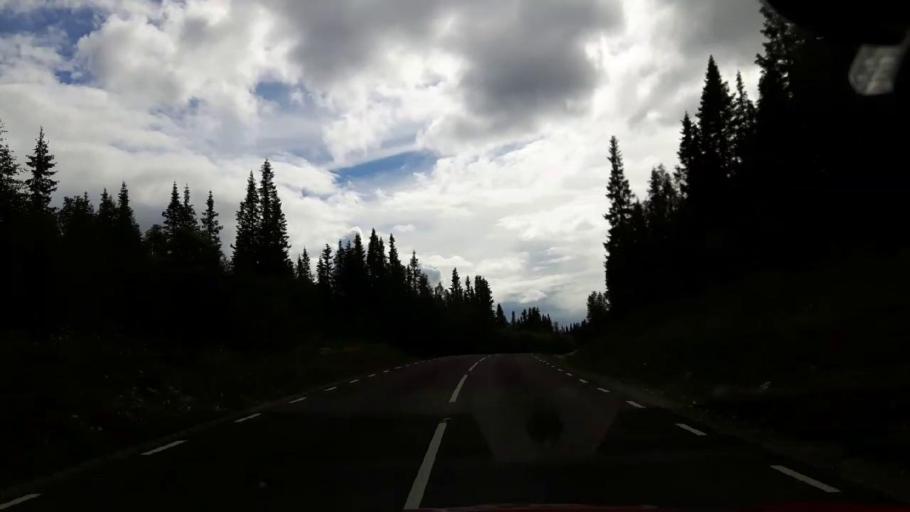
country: NO
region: Nord-Trondelag
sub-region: Royrvik
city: Royrvik
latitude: 64.8127
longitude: 14.0654
